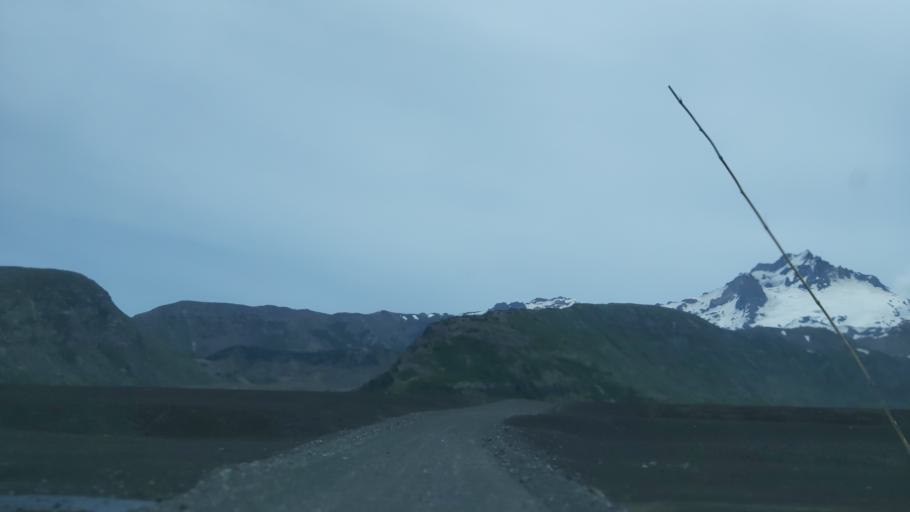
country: AR
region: Neuquen
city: Andacollo
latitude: -37.4610
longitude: -71.3083
